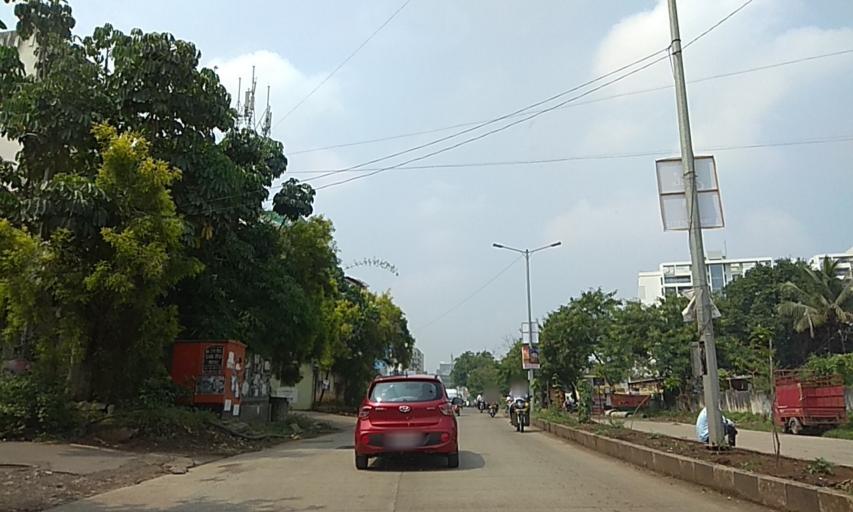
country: IN
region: Maharashtra
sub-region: Pune Division
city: Pimpri
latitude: 18.5589
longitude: 73.7783
